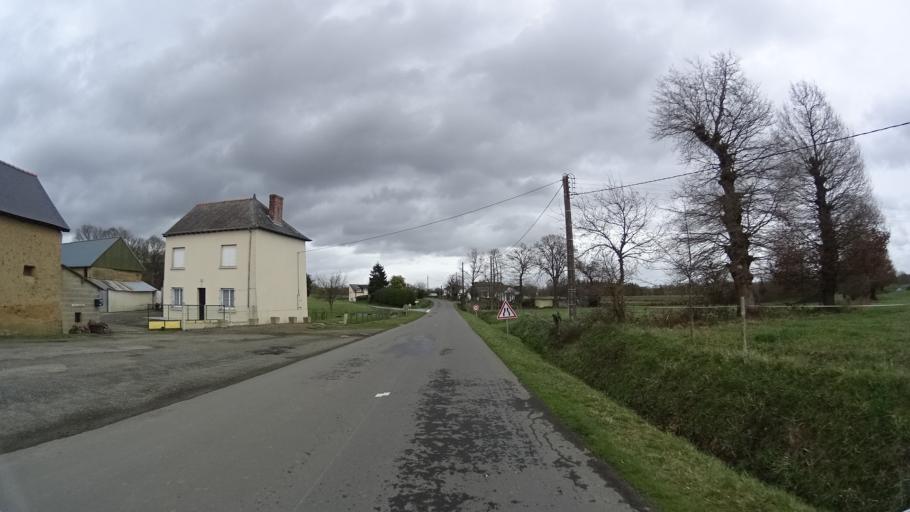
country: FR
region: Brittany
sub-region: Departement d'Ille-et-Vilaine
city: Saint-Gilles
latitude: 48.1623
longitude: -1.8318
